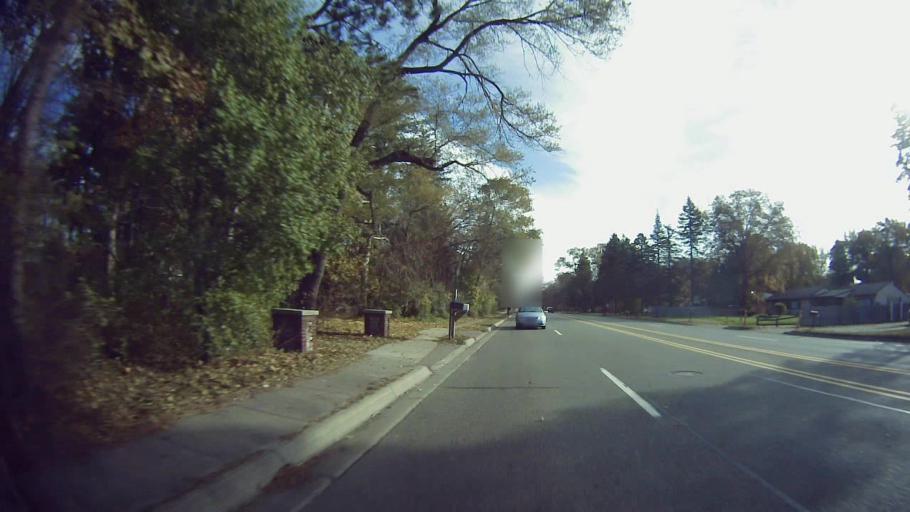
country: US
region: Michigan
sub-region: Oakland County
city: Southfield
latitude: 42.4580
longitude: -83.2563
